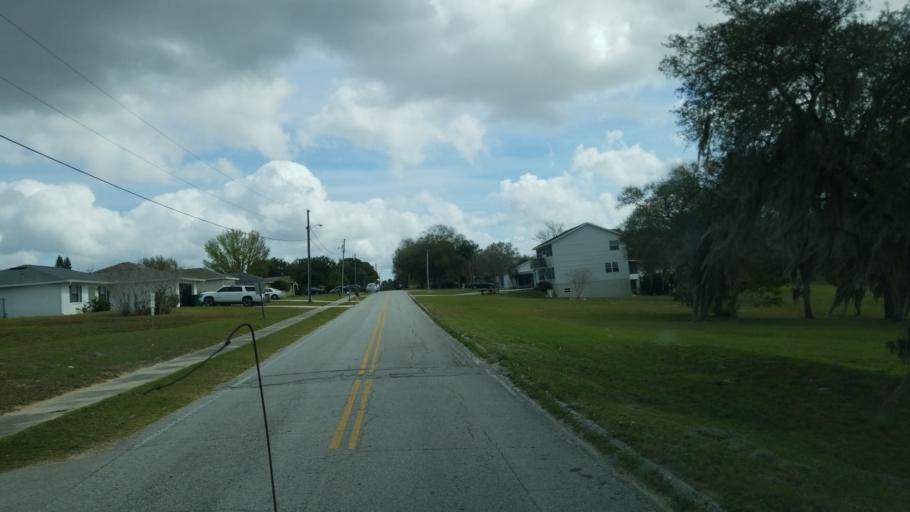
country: US
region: Florida
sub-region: Polk County
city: Dundee
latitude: 28.0260
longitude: -81.6139
